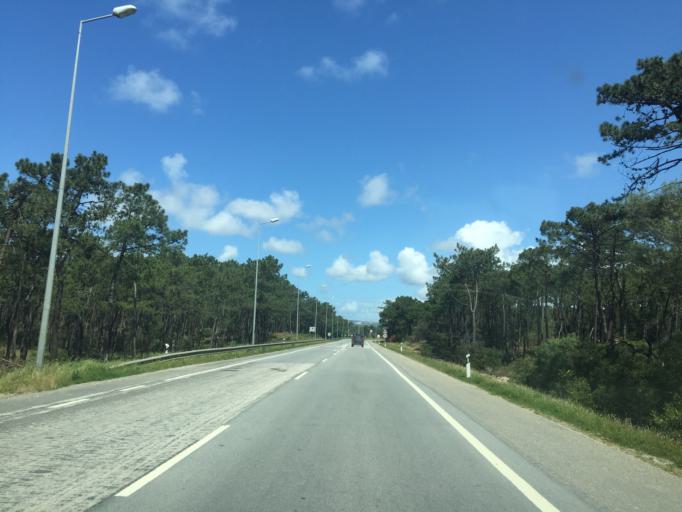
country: PT
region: Coimbra
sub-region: Figueira da Foz
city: Lavos
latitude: 40.1147
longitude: -8.8560
